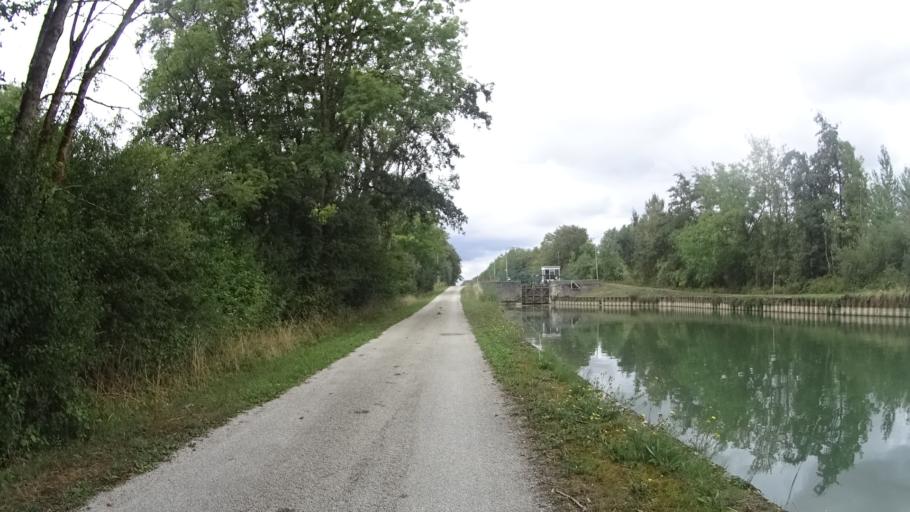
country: FR
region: Picardie
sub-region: Departement de l'Aisne
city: La Fere
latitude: 49.6994
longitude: 3.3701
